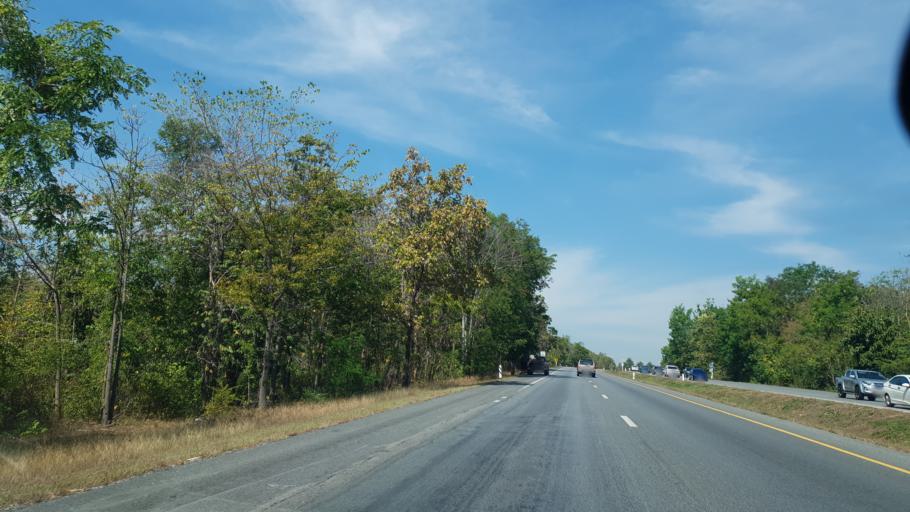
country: TH
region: Uttaradit
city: Thong Saen Khan
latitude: 17.4199
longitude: 100.2265
